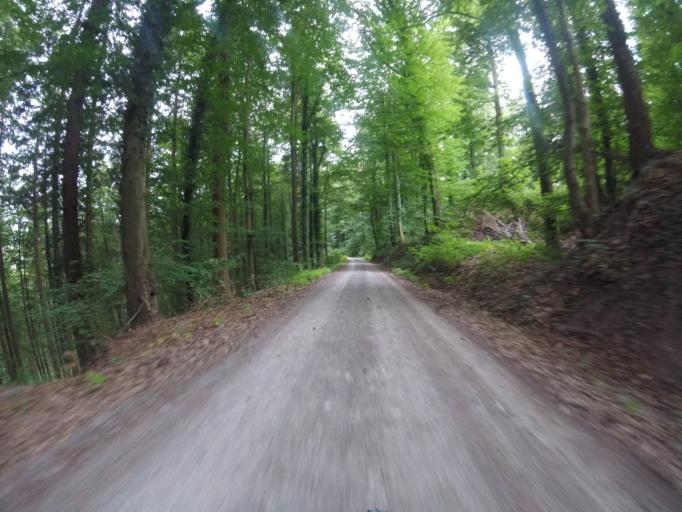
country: DE
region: Baden-Wuerttemberg
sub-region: Regierungsbezirk Stuttgart
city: Sulzbach an der Murr
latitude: 48.9704
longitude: 9.4976
